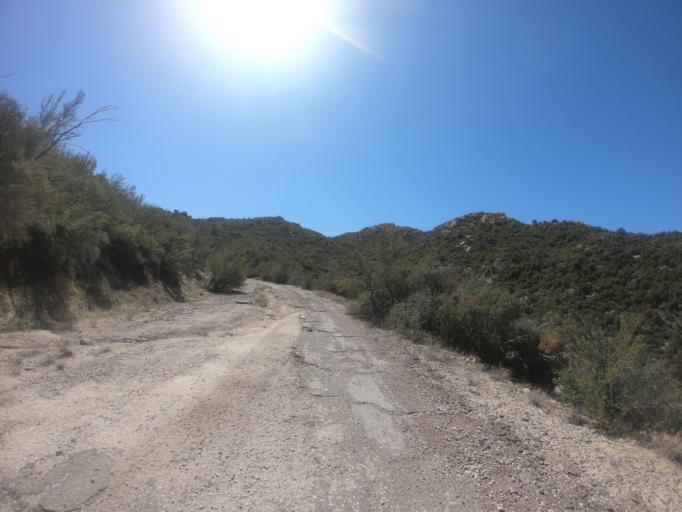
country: US
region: Arizona
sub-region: Gila County
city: Miami
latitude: 33.3567
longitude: -110.9557
